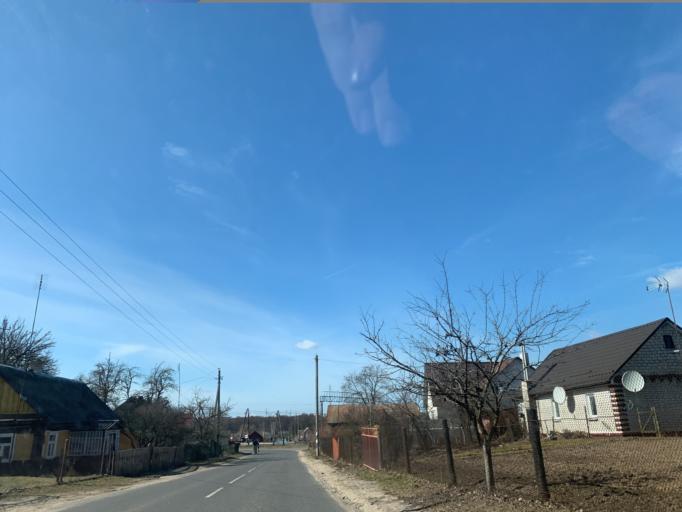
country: BY
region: Minsk
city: Haradzyeya
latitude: 53.3120
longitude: 26.5369
